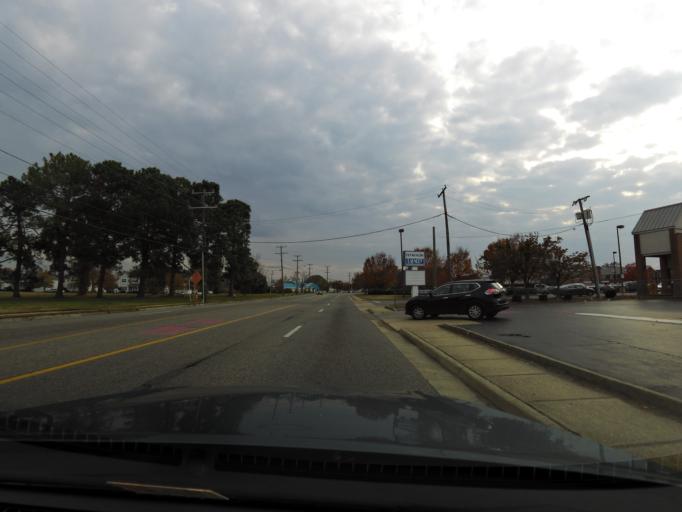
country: US
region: Virginia
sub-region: City of Hampton
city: Hampton
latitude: 37.0125
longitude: -76.3531
